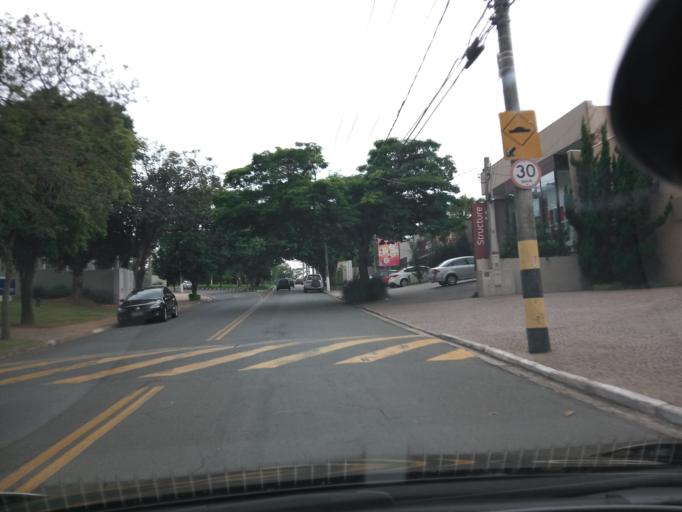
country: BR
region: Sao Paulo
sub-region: Campinas
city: Campinas
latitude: -22.8953
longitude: -47.0320
